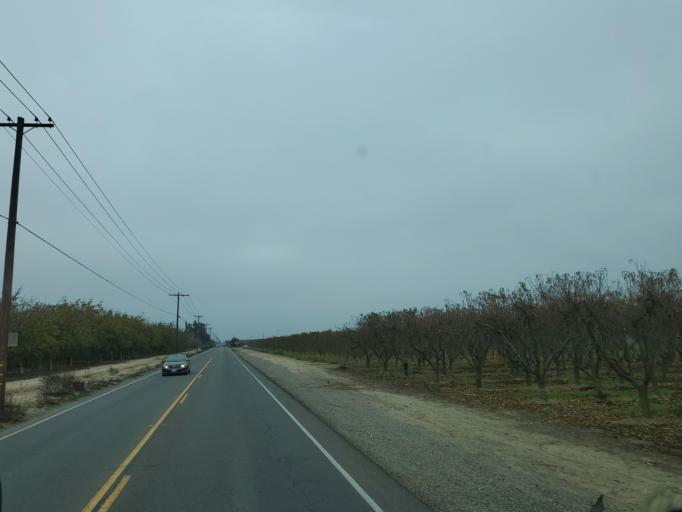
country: US
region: California
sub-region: Stanislaus County
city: Hughson
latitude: 37.5512
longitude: -120.8691
